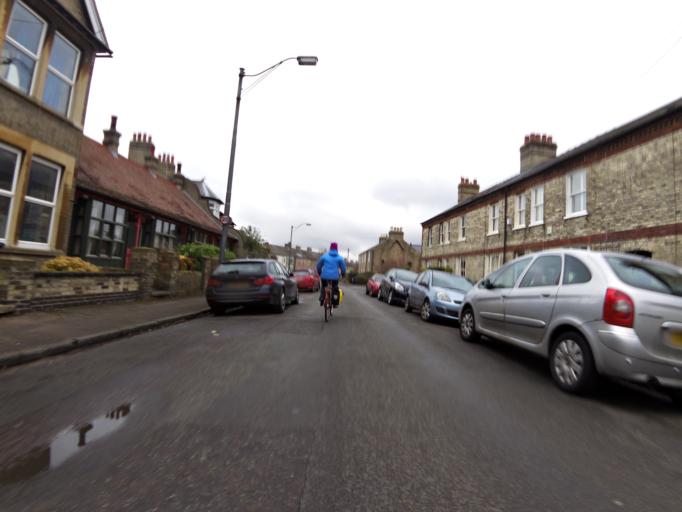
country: GB
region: England
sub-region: Cambridgeshire
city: Cambridge
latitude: 52.2171
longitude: 0.1411
